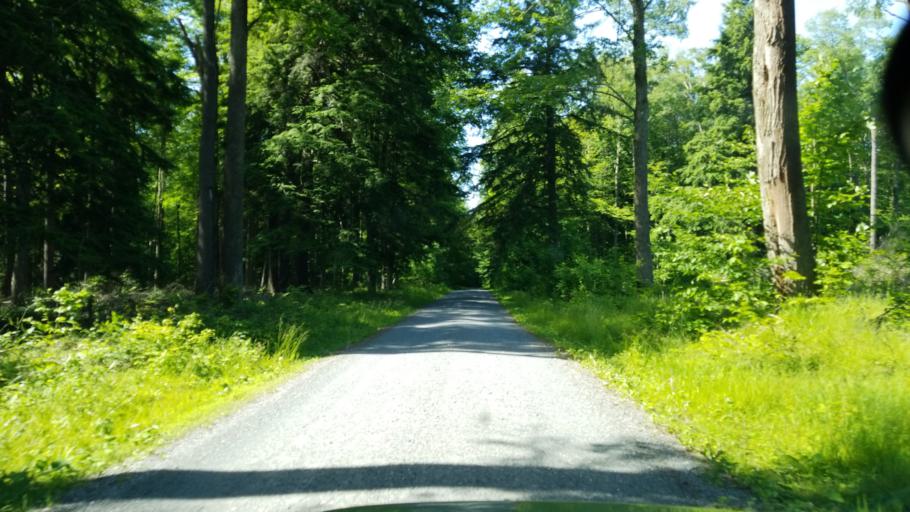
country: US
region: Pennsylvania
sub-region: Clearfield County
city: Clearfield
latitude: 41.1992
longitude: -78.4833
